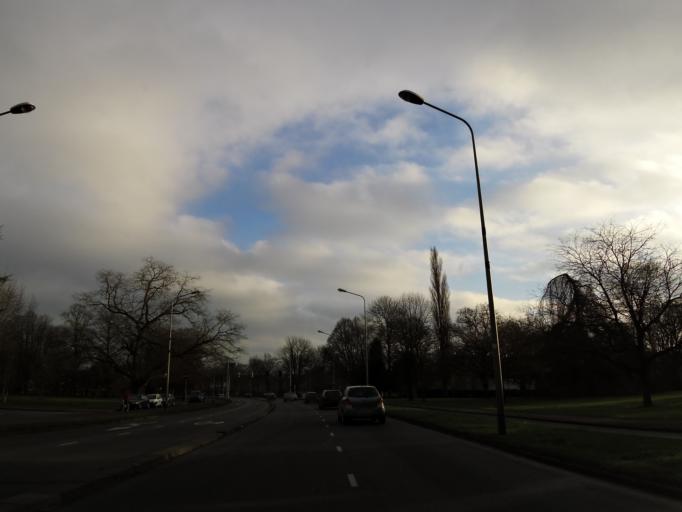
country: NL
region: Limburg
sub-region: Gemeente Maastricht
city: Maastricht
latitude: 50.8438
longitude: 5.6820
